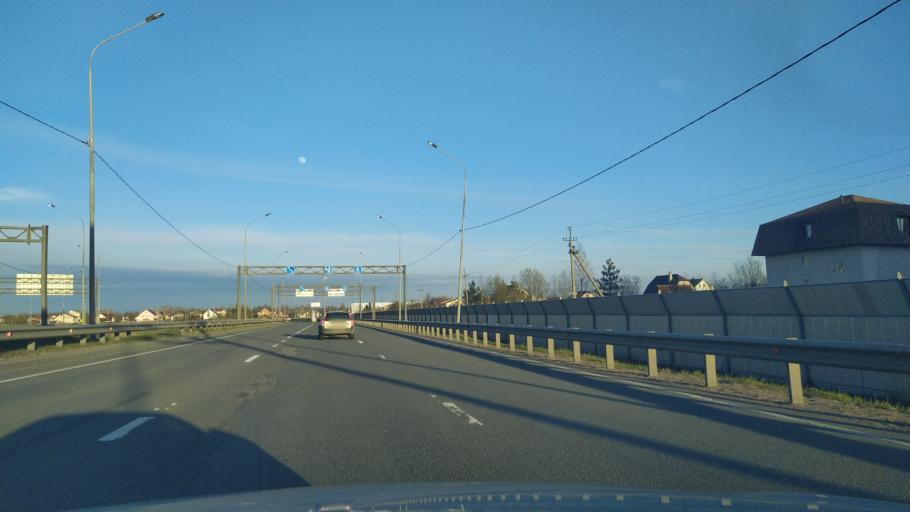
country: RU
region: St.-Petersburg
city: Aleksandrovskaya
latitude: 59.7416
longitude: 30.3181
